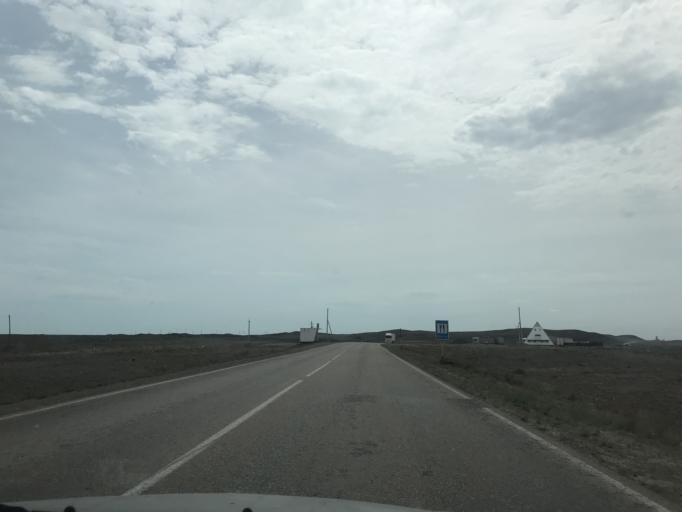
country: KZ
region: Zhambyl
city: Mynaral
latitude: 45.4526
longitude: 73.5990
